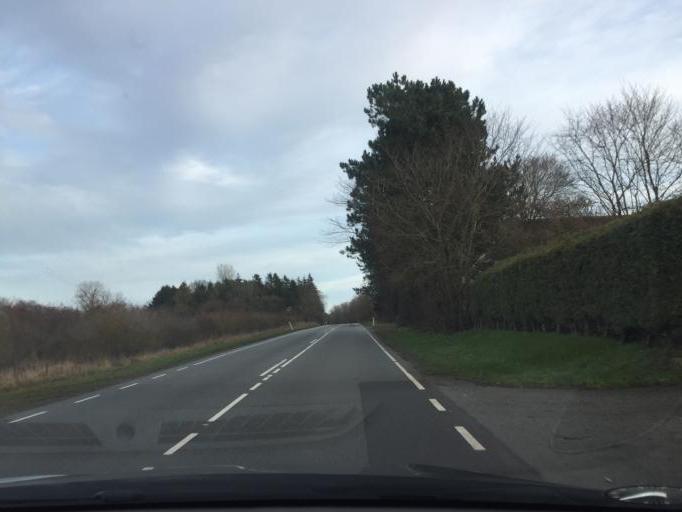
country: DK
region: South Denmark
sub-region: Faaborg-Midtfyn Kommune
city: Ringe
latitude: 55.2096
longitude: 10.4144
